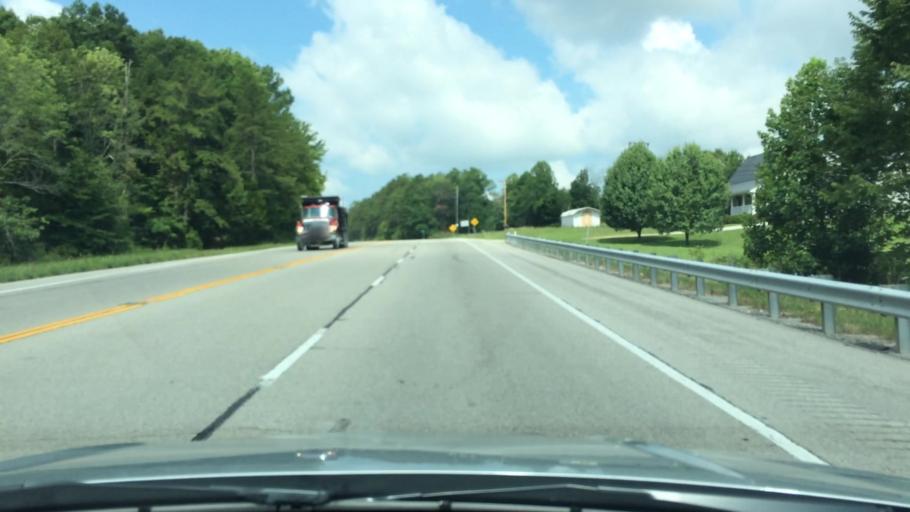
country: US
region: Kentucky
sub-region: Pulaski County
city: Somerset
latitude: 36.9460
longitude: -84.5598
